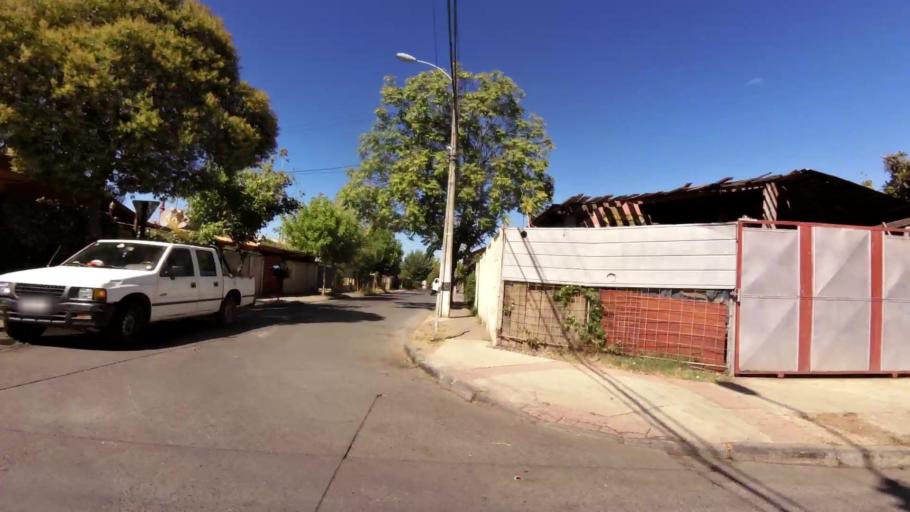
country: CL
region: O'Higgins
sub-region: Provincia de Cachapoal
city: Rancagua
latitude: -34.1690
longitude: -70.7041
